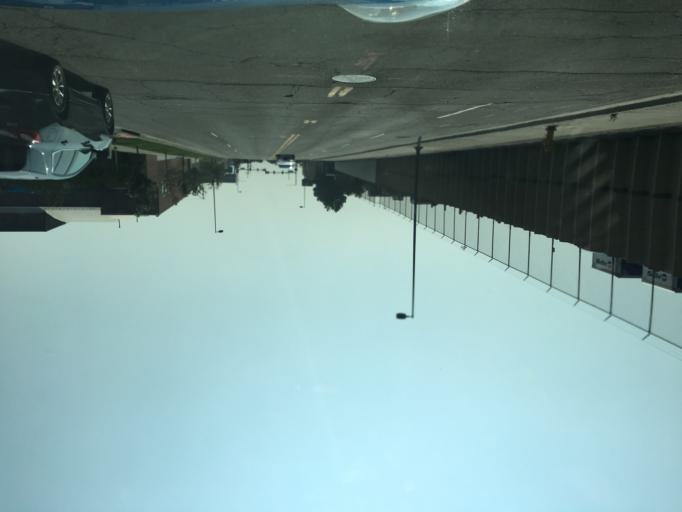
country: US
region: Colorado
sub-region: Denver County
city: Denver
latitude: 39.7745
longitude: -104.9774
